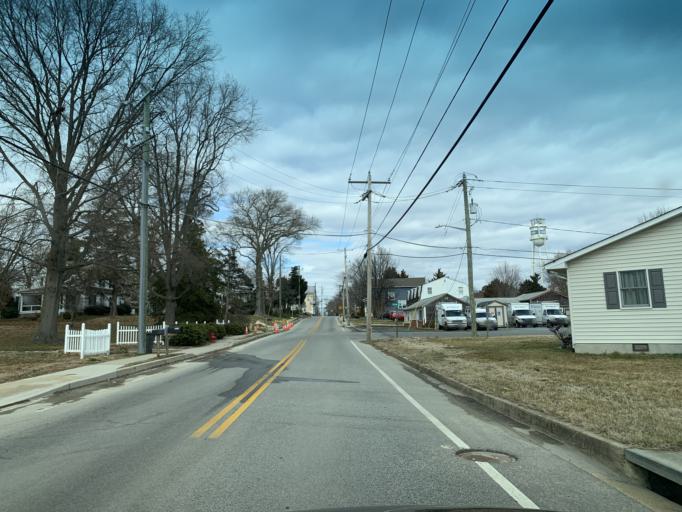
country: US
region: Maryland
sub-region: Queen Anne's County
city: Grasonville
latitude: 38.9891
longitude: -76.1589
